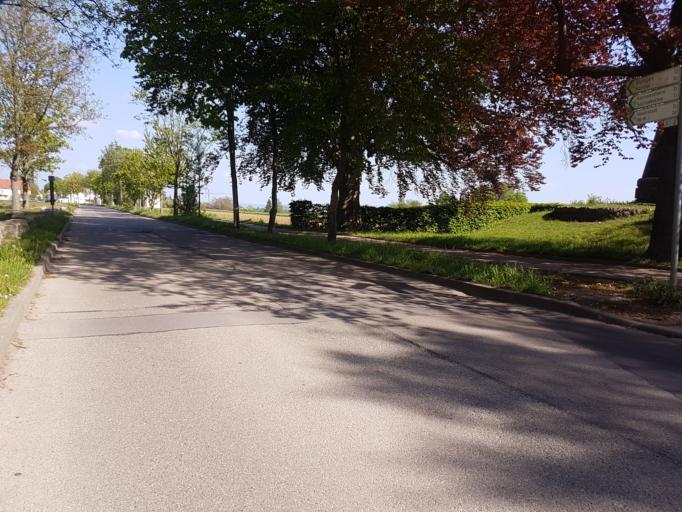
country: DE
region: Baden-Wuerttemberg
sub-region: Regierungsbezirk Stuttgart
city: Ludwigsburg
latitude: 48.8845
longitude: 9.1763
